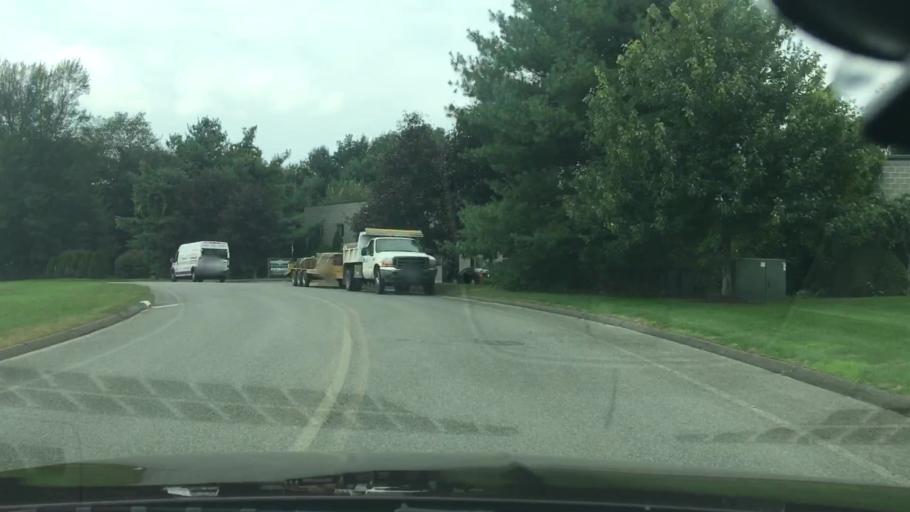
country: US
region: Connecticut
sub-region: Hartford County
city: South Windsor
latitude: 41.8601
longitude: -72.5972
